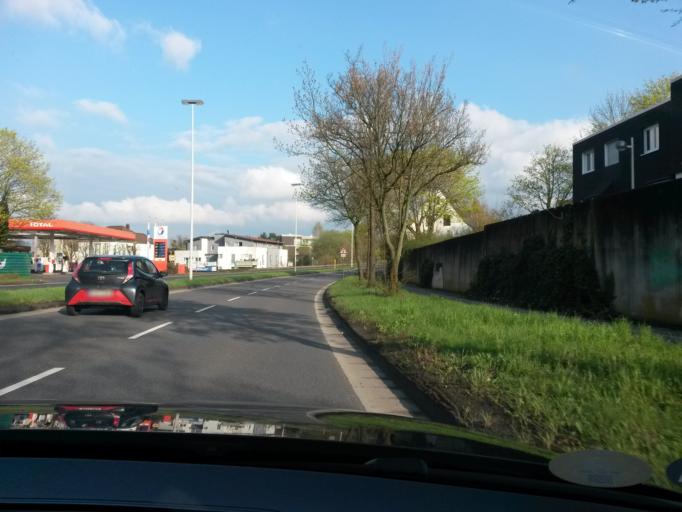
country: DE
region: North Rhine-Westphalia
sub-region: Regierungsbezirk Koln
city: Alfter
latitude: 50.7121
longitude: 7.0396
